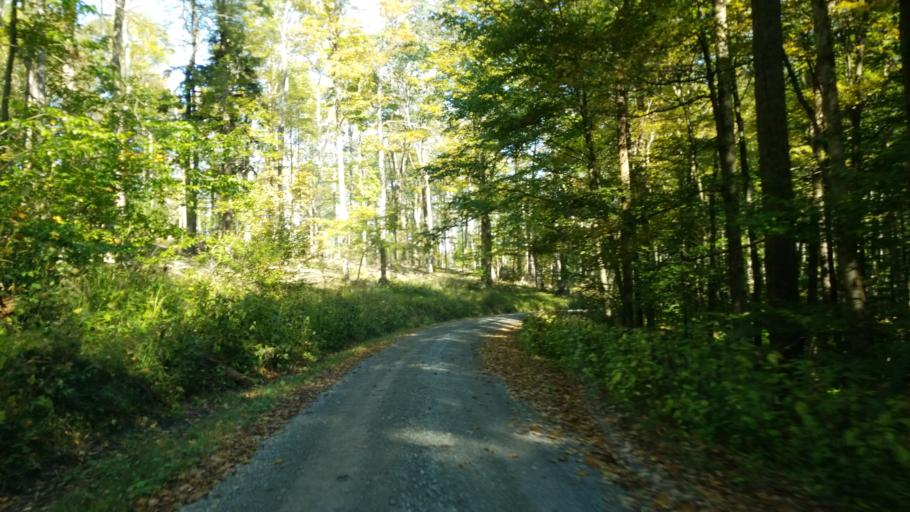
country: US
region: Pennsylvania
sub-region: Clearfield County
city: Treasure Lake
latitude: 41.1424
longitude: -78.5749
